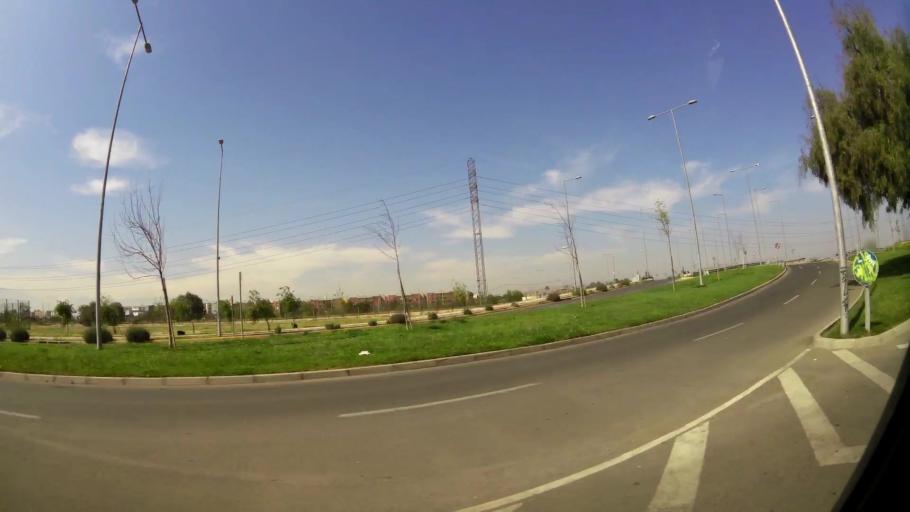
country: CL
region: Santiago Metropolitan
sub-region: Provincia de Santiago
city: Lo Prado
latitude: -33.4835
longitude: -70.7422
